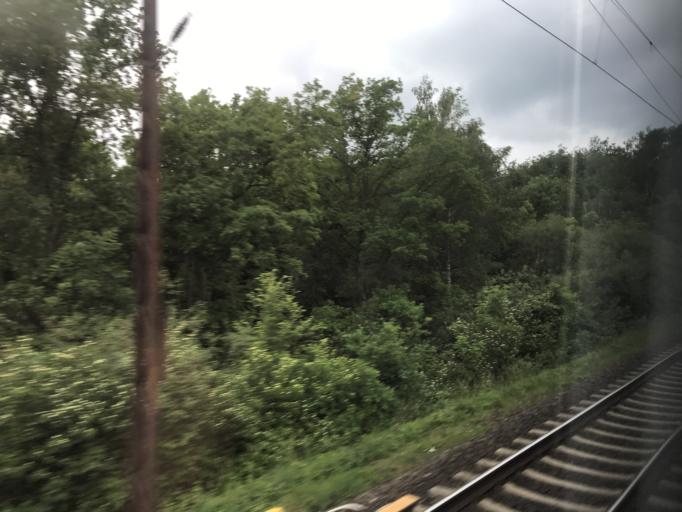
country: DE
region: Bavaria
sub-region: Swabia
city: Guenzburg
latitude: 48.4582
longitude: 10.2643
